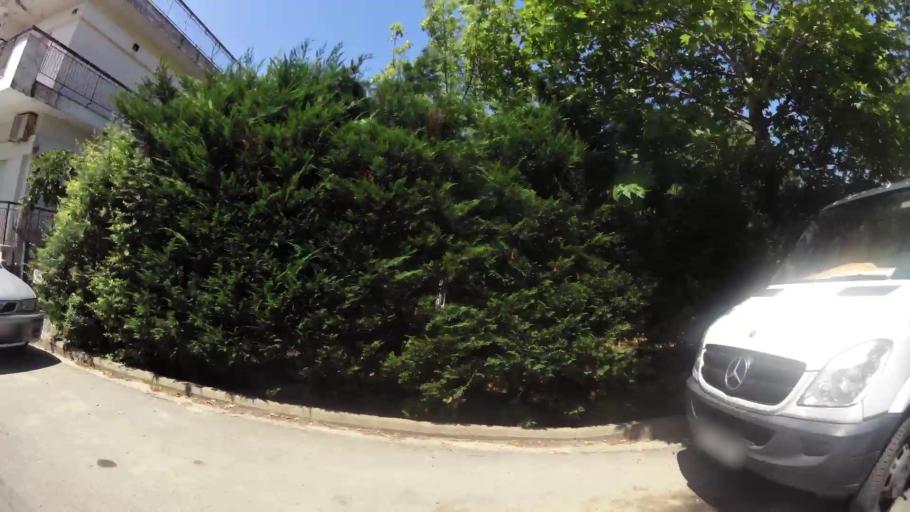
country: GR
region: Central Macedonia
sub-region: Nomos Thessalonikis
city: Nea Michaniona
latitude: 40.4965
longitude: 22.8197
